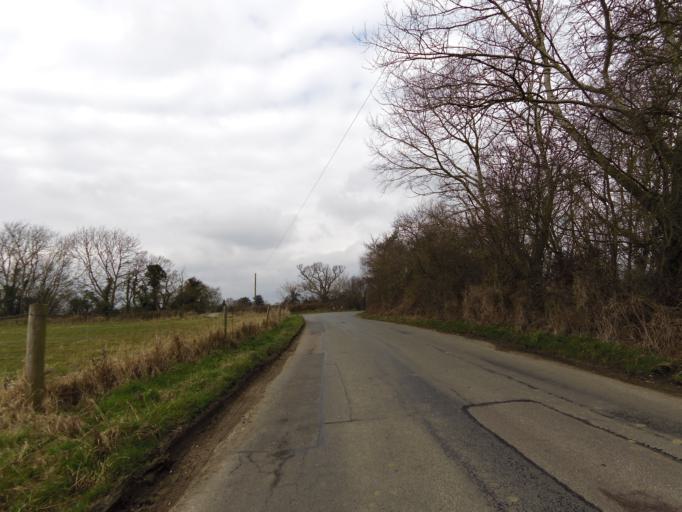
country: GB
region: England
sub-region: Suffolk
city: Halesworth
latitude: 52.3975
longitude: 1.5396
